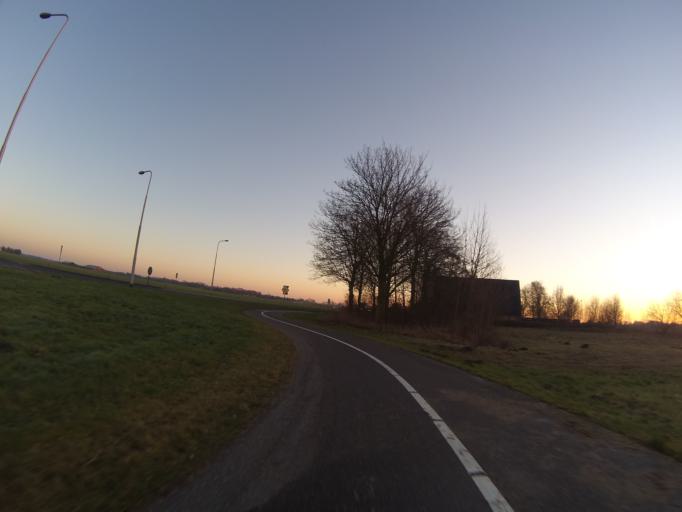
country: NL
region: Drenthe
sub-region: Gemeente Emmen
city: Schoonebeek
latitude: 52.7222
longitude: 6.8766
